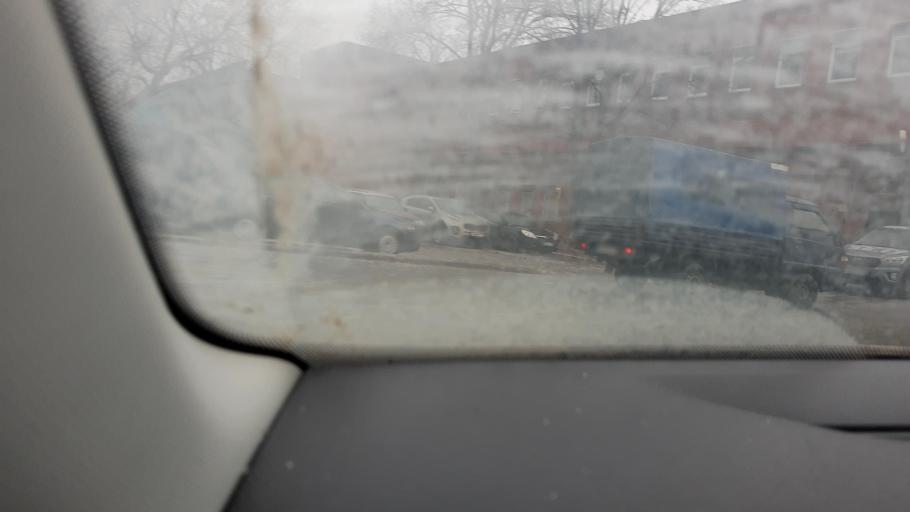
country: RU
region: Moscow
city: Tsaritsyno
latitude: 55.6227
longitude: 37.6361
